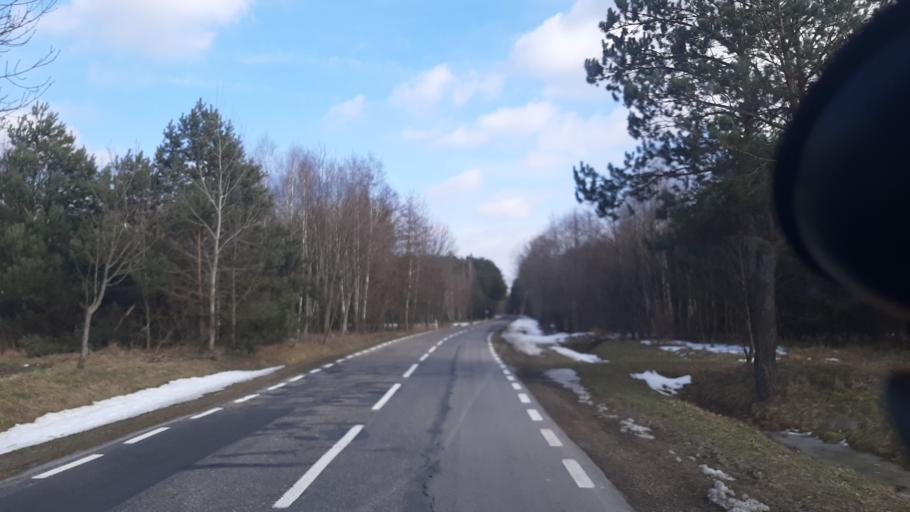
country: PL
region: Lublin Voivodeship
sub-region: Powiat parczewski
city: Sosnowica
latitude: 51.4966
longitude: 23.1785
